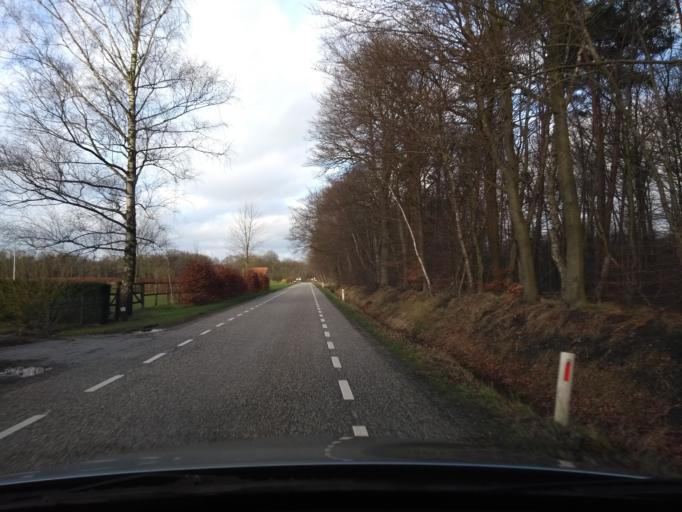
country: NL
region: Overijssel
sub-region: Gemeente Haaksbergen
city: Haaksbergen
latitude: 52.1164
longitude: 6.7516
